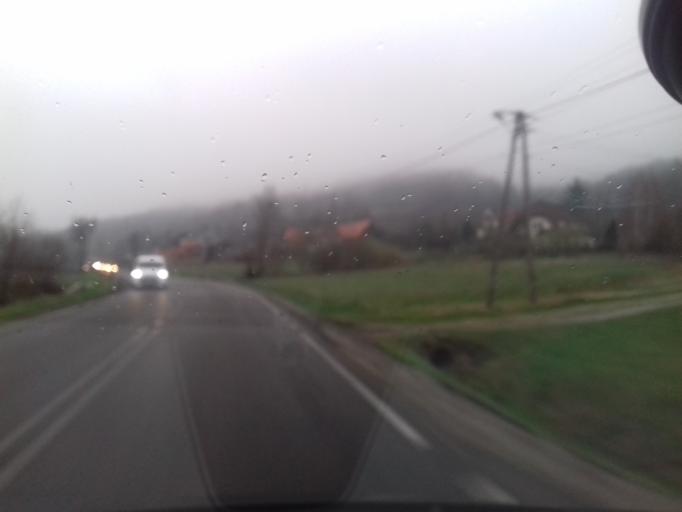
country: PL
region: Lesser Poland Voivodeship
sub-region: Powiat limanowski
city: Dobra
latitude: 49.7042
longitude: 20.2111
